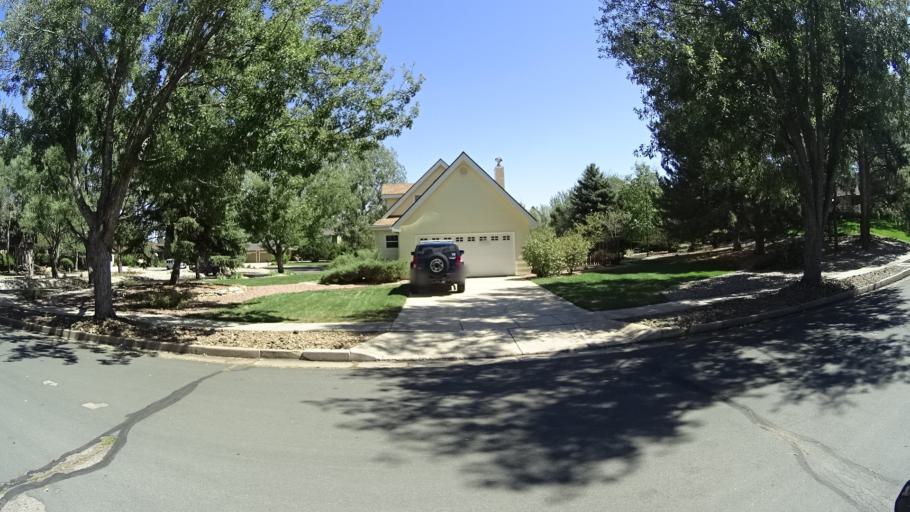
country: US
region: Colorado
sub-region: El Paso County
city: Colorado Springs
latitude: 38.7899
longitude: -104.8293
